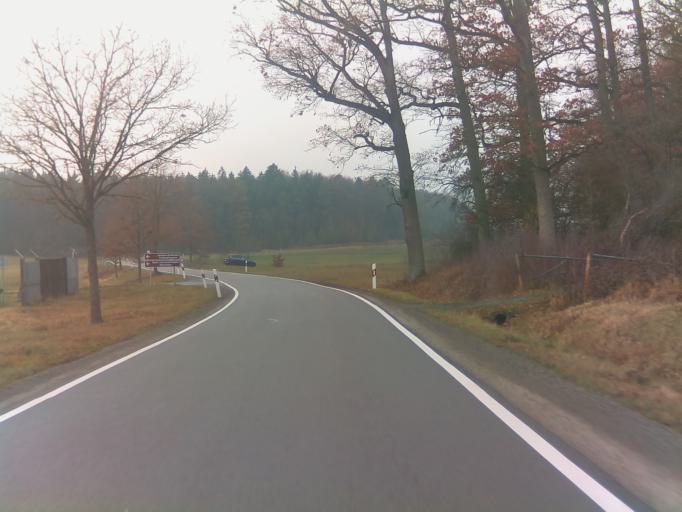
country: DE
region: Bavaria
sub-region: Regierungsbezirk Unterfranken
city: Hochheim
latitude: 50.4064
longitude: 10.4377
